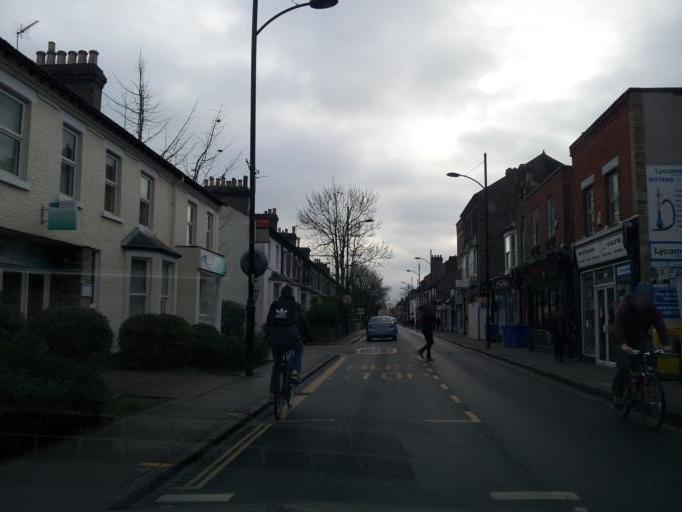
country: GB
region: England
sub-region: Cambridgeshire
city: Cambridge
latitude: 52.2009
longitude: 0.1351
